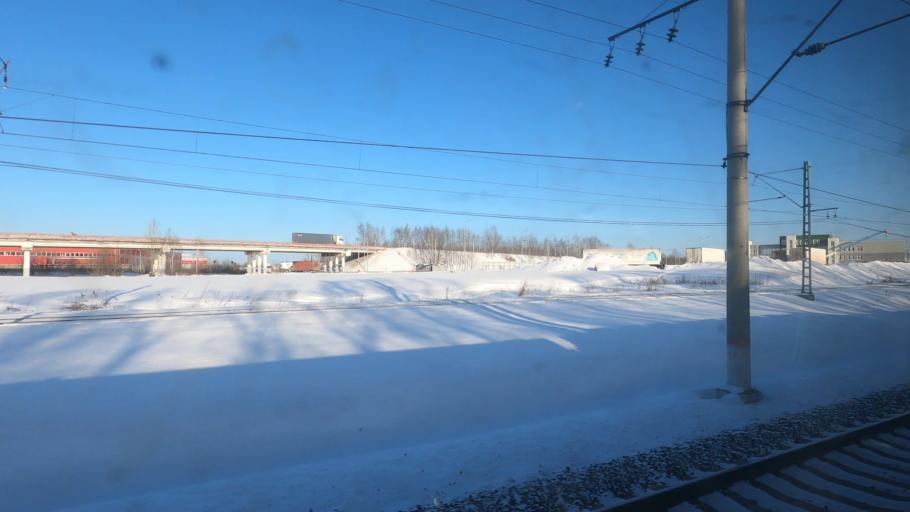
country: RU
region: Moskovskaya
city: Elektrougli
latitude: 55.7245
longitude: 38.2224
